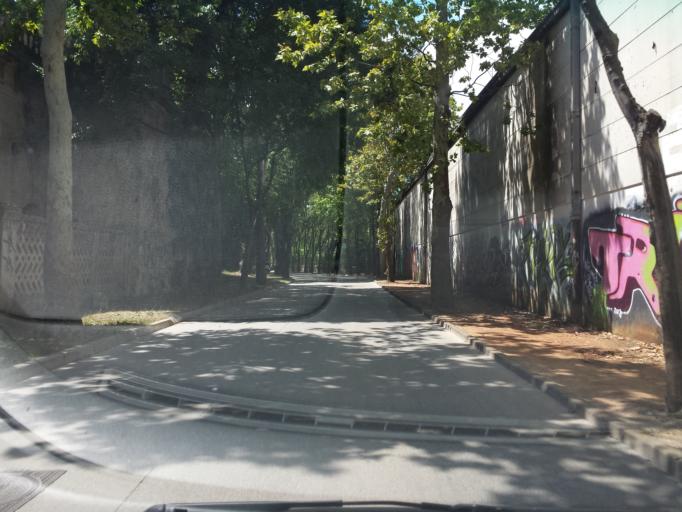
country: HR
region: Istarska
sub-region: Grad Pula
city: Pula
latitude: 44.8624
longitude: 13.8316
